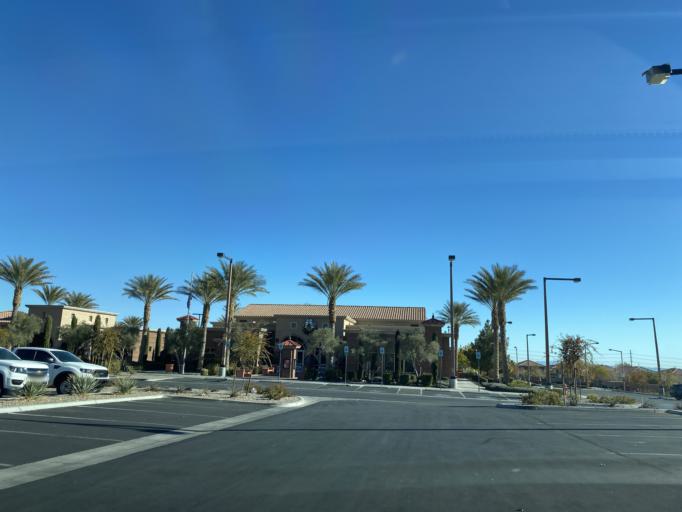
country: US
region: Nevada
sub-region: Clark County
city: Summerlin South
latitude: 36.1687
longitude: -115.3449
